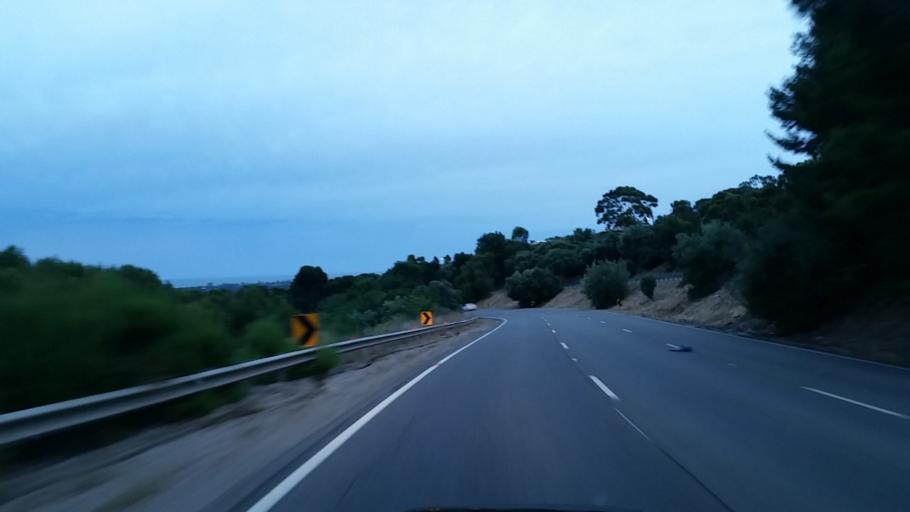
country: AU
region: South Australia
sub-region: Onkaparinga
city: Bedford Park
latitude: -35.0353
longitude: 138.5590
